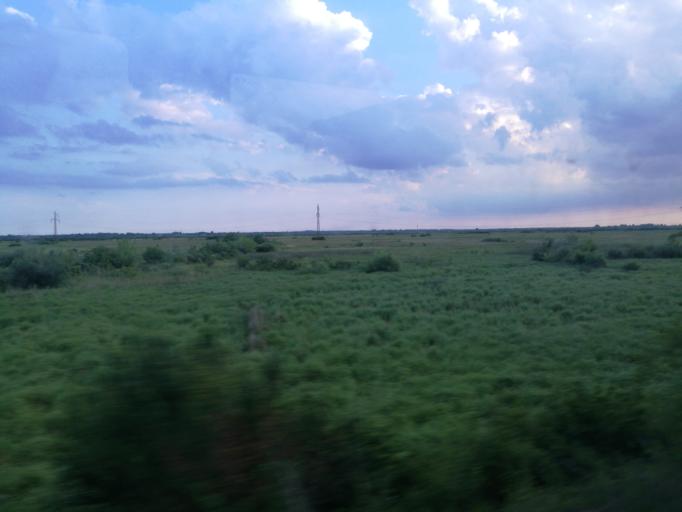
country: RO
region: Dambovita
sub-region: Comuna Produlesti
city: Costestii din Deal
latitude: 44.6760
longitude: 25.4918
